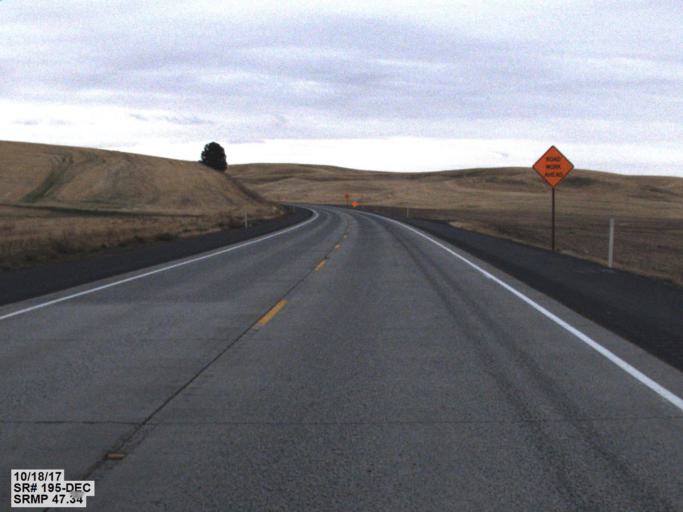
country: US
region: Washington
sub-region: Whitman County
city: Colfax
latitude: 46.9965
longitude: -117.3540
